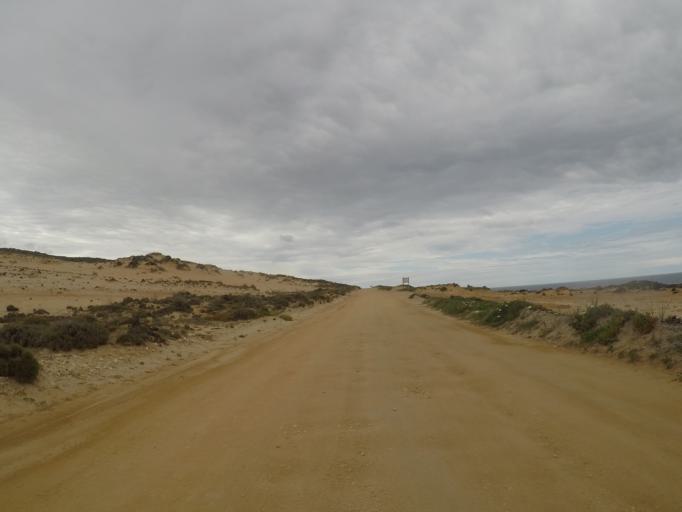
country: PT
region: Beja
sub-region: Odemira
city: Vila Nova de Milfontes
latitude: 37.6466
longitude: -8.8052
